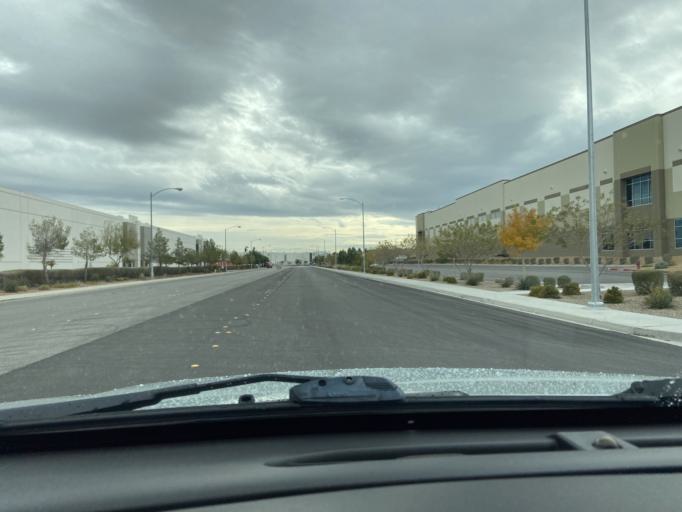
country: US
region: Nevada
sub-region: Clark County
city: North Las Vegas
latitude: 36.2456
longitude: -115.1079
